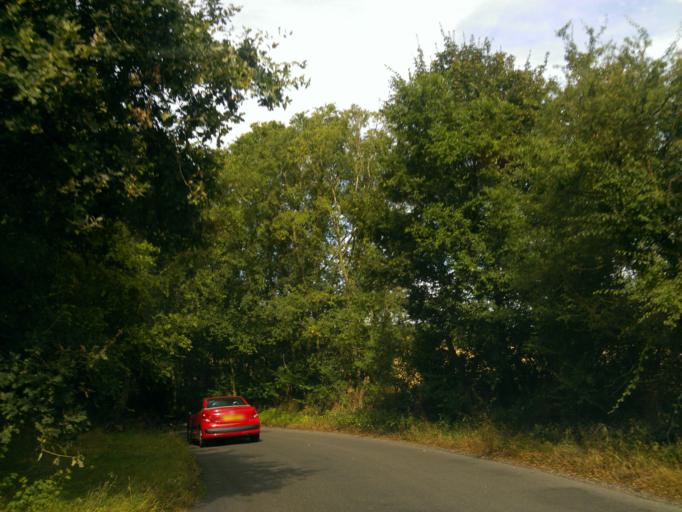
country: GB
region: England
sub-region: Essex
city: Sible Hedingham
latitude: 51.9808
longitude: 0.6135
